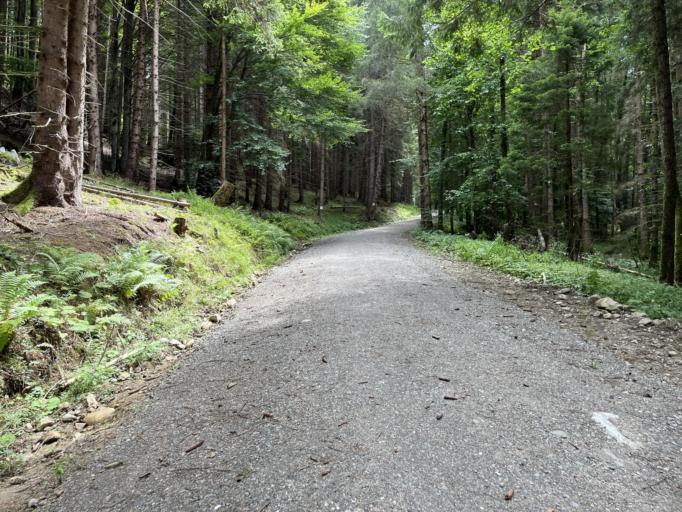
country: AT
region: Carinthia
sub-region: Politischer Bezirk Spittal an der Drau
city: Millstatt
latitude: 46.7925
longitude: 13.5499
